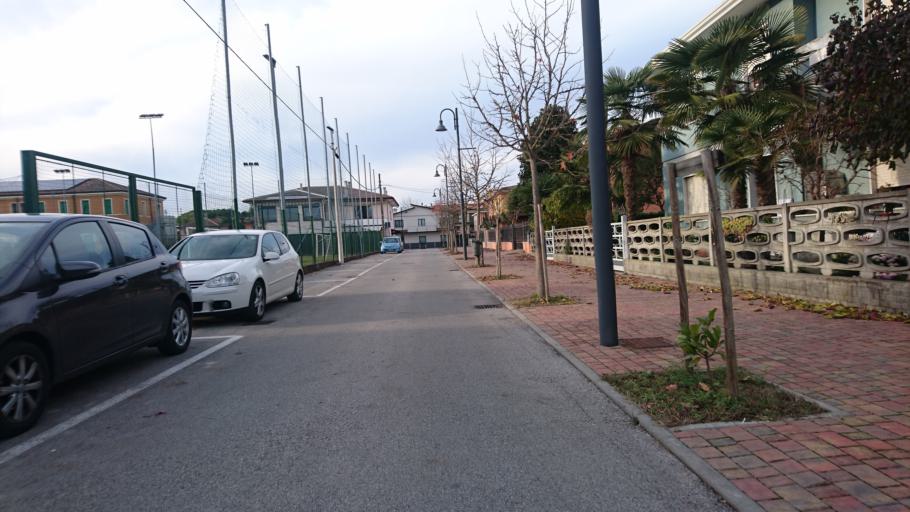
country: IT
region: Veneto
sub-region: Provincia di Padova
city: Polverara
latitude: 45.3107
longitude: 11.9590
